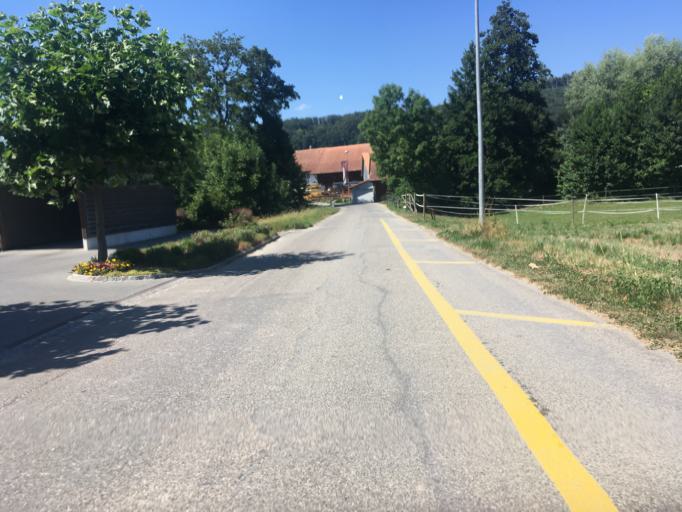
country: CH
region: Bern
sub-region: Biel/Bienne District
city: Meinisberg
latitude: 47.1136
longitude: 7.3580
